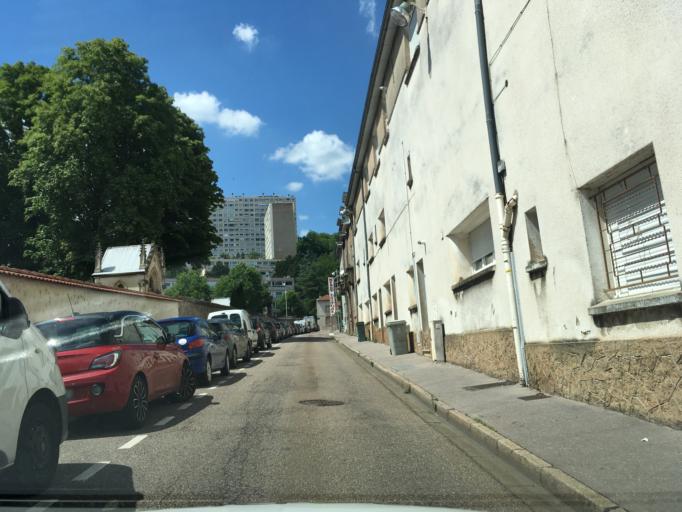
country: FR
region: Lorraine
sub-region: Departement de Meurthe-et-Moselle
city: Maxeville
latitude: 48.6911
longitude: 6.1647
